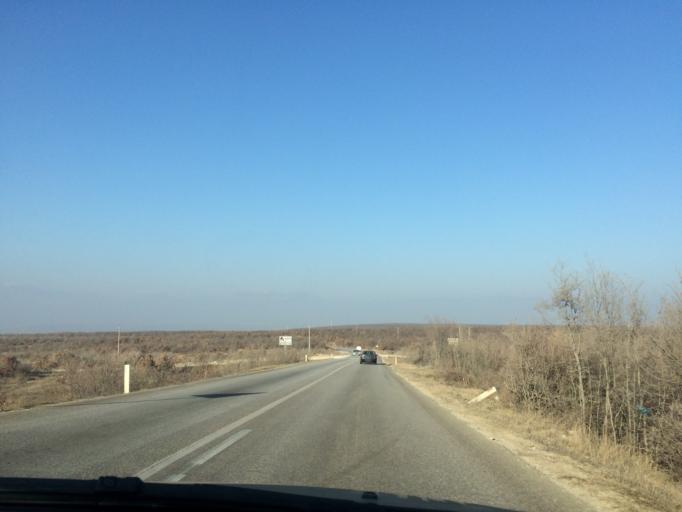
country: XK
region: Pec
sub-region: Komuna e Klines
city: Klina
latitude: 42.5958
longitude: 20.6284
